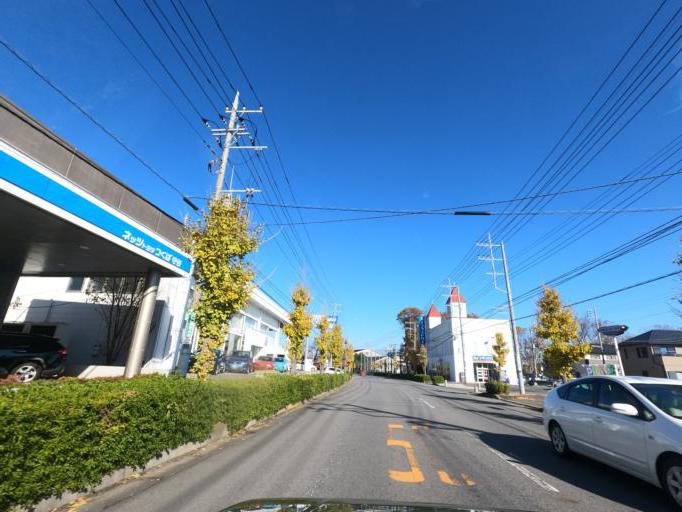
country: JP
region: Ibaraki
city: Mitsukaido
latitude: 35.9791
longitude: 139.9756
